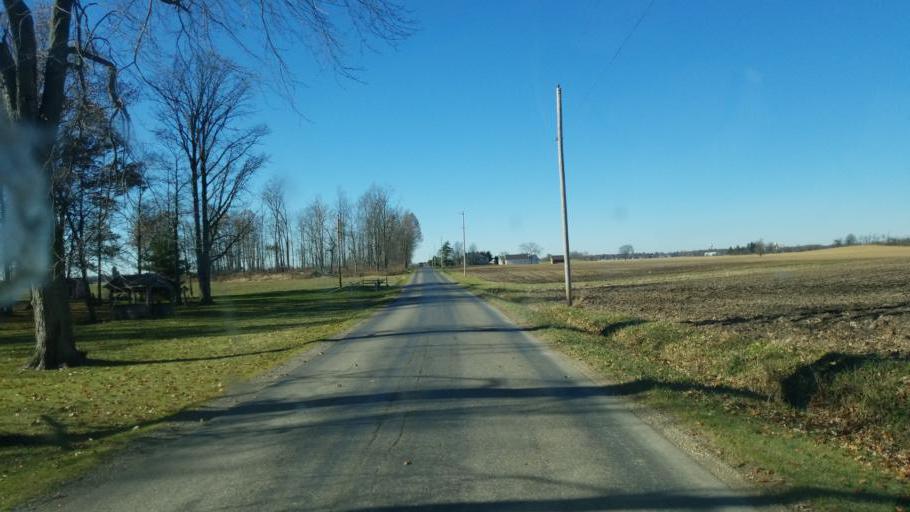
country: US
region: Ohio
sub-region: Huron County
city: Greenwich
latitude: 40.9602
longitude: -82.5725
